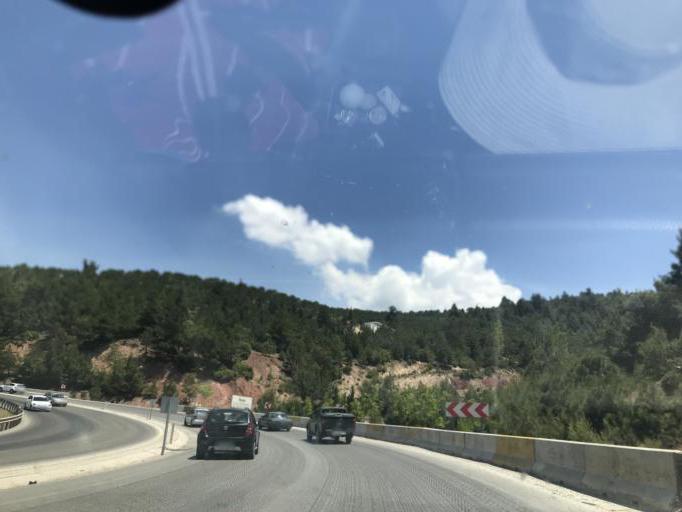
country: TR
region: Denizli
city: Denizli
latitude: 37.7294
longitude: 29.1705
